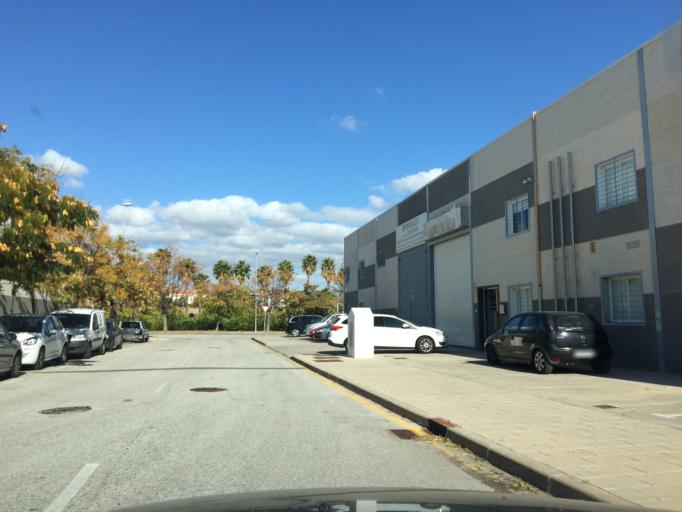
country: ES
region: Andalusia
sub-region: Provincia de Malaga
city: Alhaurin de la Torre
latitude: 36.7334
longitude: -4.5430
